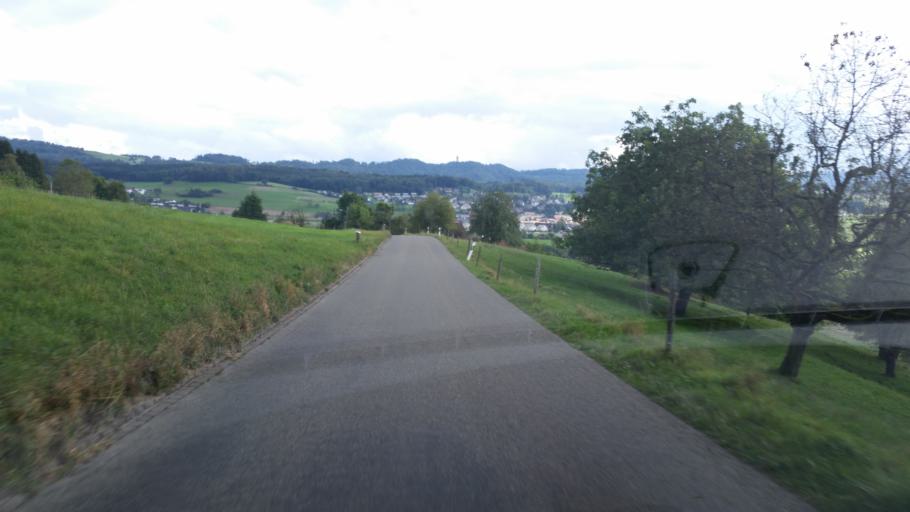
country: CH
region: Zurich
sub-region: Bezirk Affoltern
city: Bonstetten
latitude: 47.3179
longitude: 8.4494
